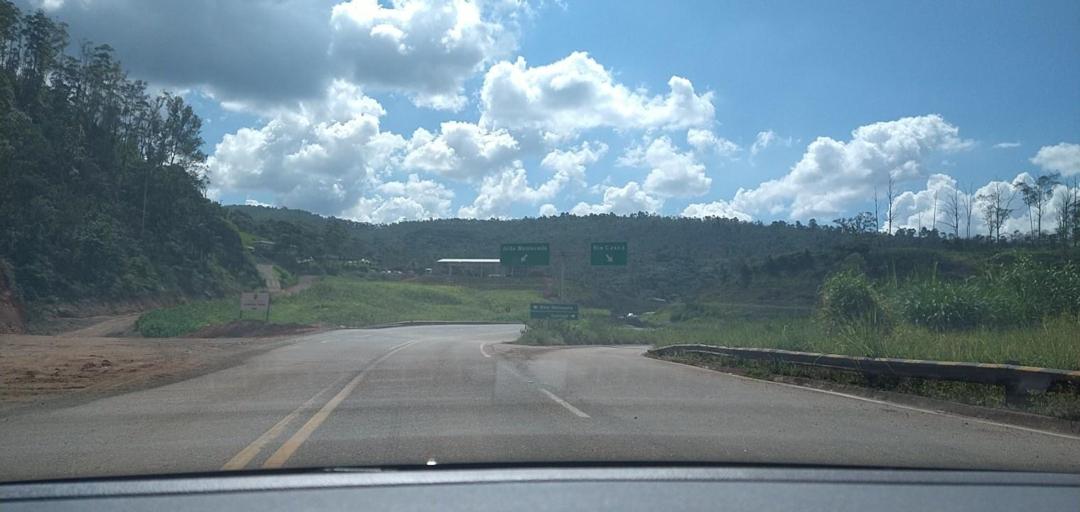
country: BR
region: Minas Gerais
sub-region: Joao Monlevade
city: Joao Monlevade
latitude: -19.8656
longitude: -43.1211
